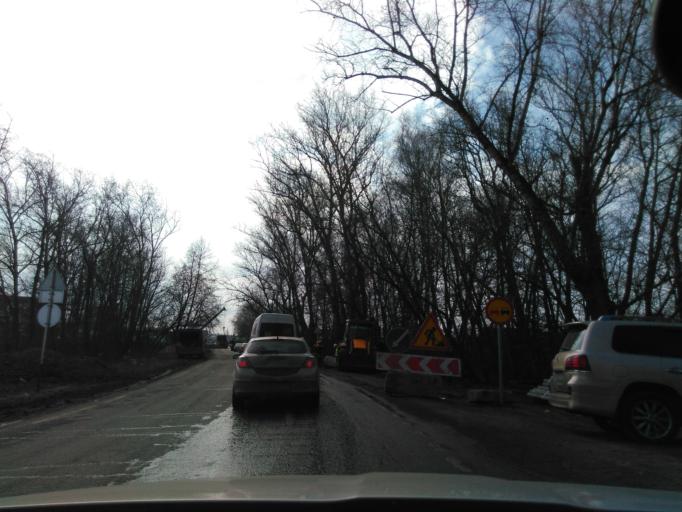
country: RU
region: Moscow
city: Severnyy
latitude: 55.9587
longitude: 37.5319
